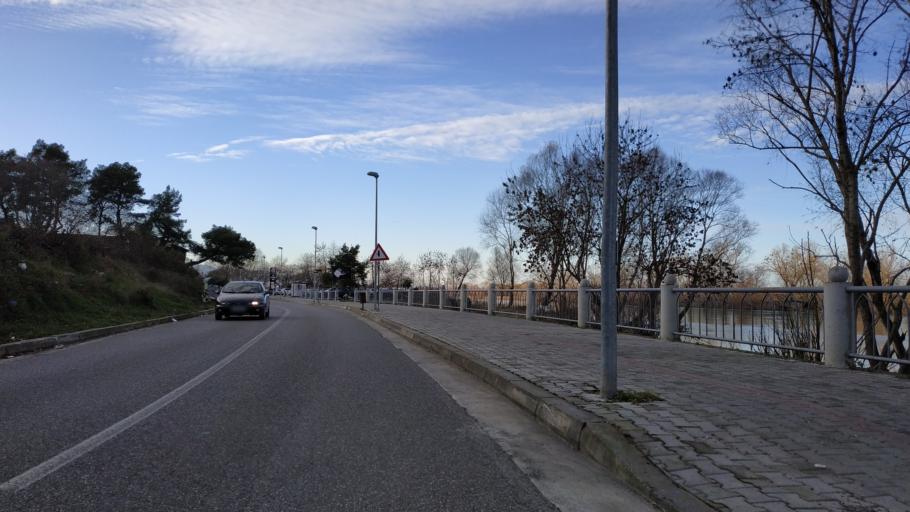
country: AL
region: Shkoder
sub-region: Rrethi i Shkodres
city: Shkoder
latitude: 42.0539
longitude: 19.4899
